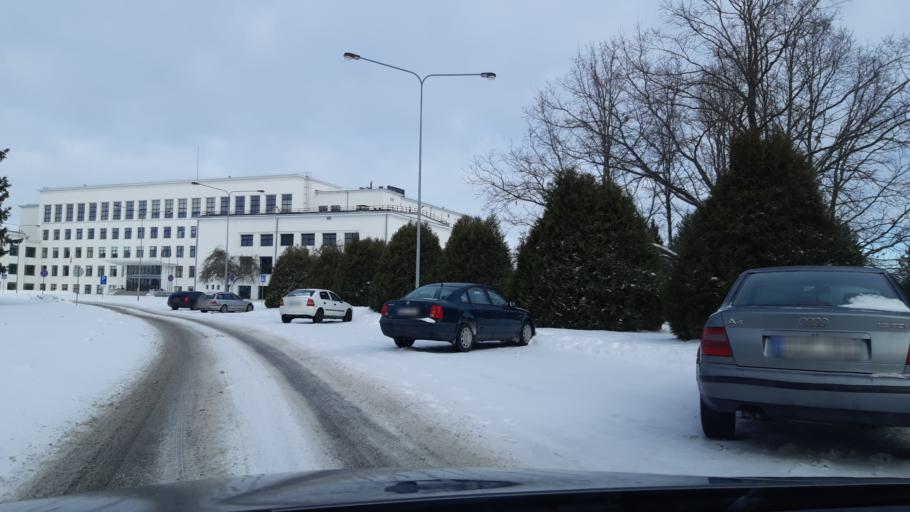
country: LT
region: Kauno apskritis
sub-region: Kauno rajonas
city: Akademija (Kaunas)
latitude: 54.8924
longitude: 23.8355
